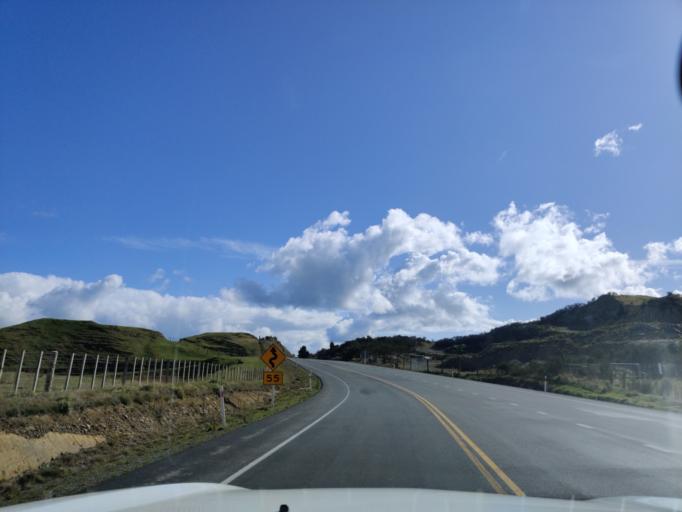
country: NZ
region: Manawatu-Wanganui
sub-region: Palmerston North City
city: Palmerston North
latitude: -40.2914
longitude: 175.8030
